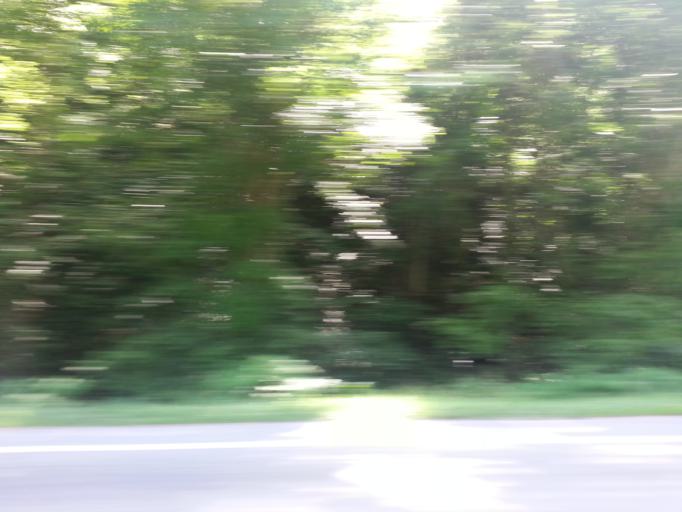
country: US
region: Virginia
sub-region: Lee County
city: Pennington Gap
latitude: 36.7576
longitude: -83.0127
